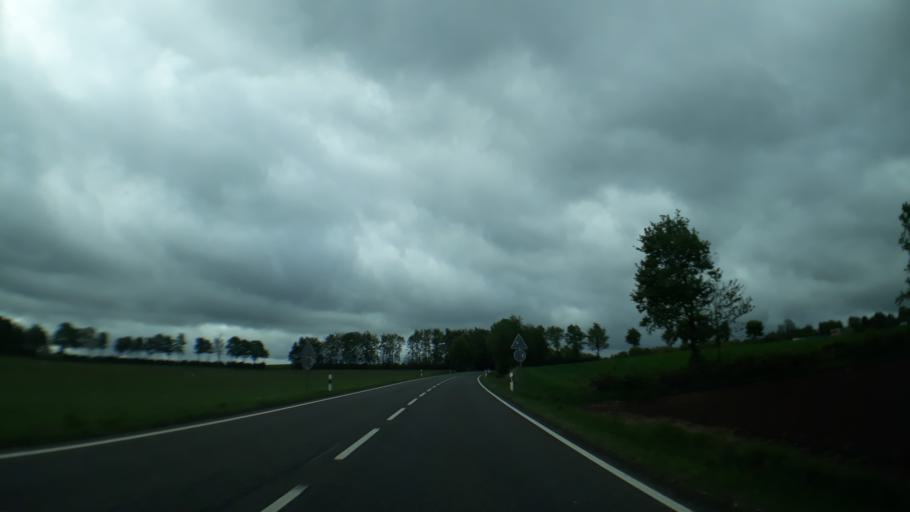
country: DE
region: North Rhine-Westphalia
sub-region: Regierungsbezirk Koln
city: Kall
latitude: 50.5427
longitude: 6.5966
